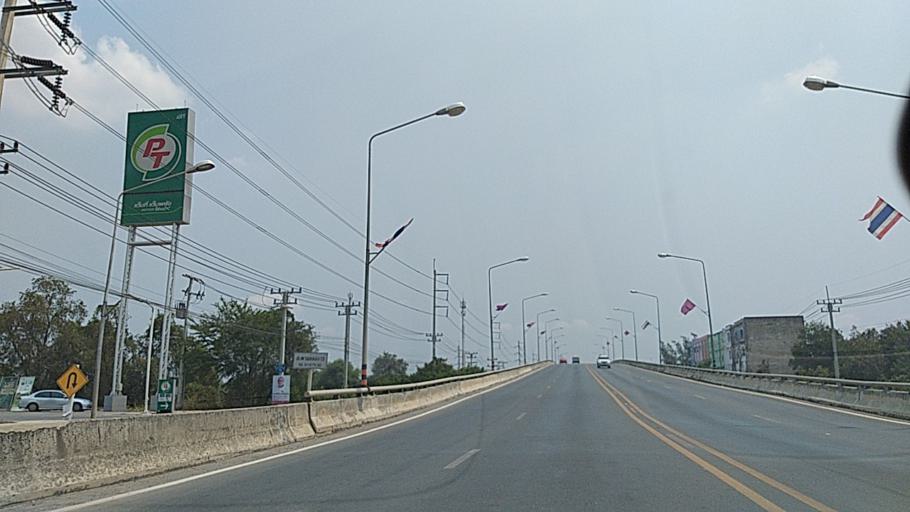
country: TH
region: Bangkok
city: Nong Chok
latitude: 13.9607
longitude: 100.8931
